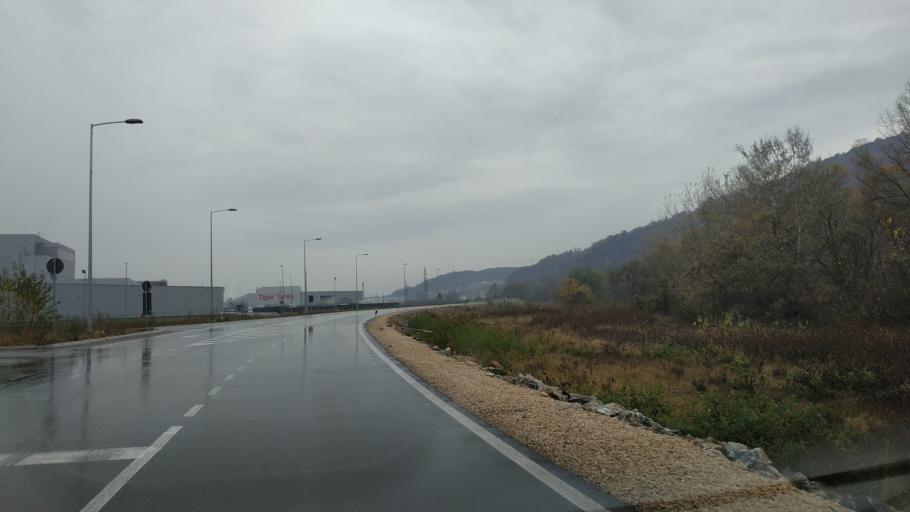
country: RS
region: Central Serbia
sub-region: Pirotski Okrug
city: Pirot
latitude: 43.1788
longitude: 22.5711
